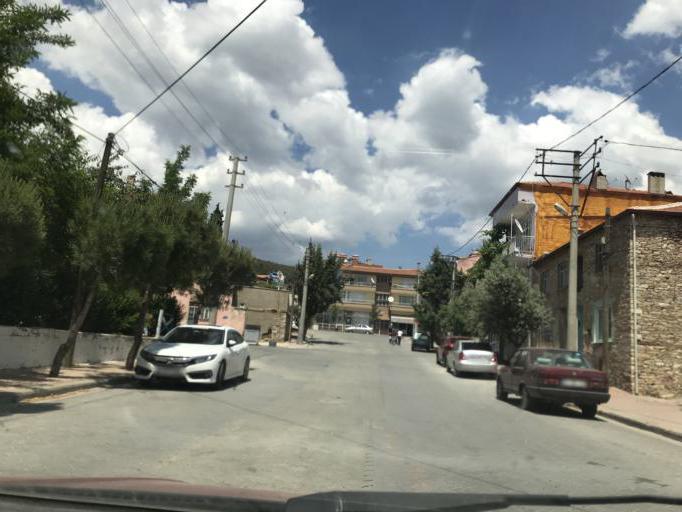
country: TR
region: Denizli
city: Tavas
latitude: 37.5744
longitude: 29.0658
